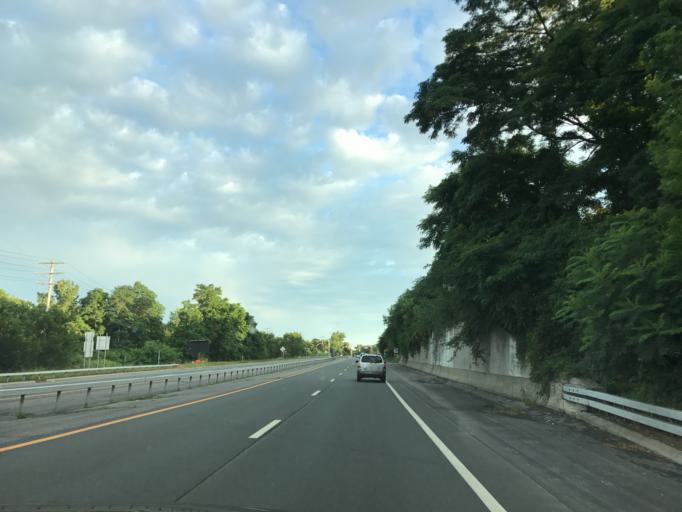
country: US
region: New York
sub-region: Albany County
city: Cohoes
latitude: 42.7722
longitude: -73.6972
